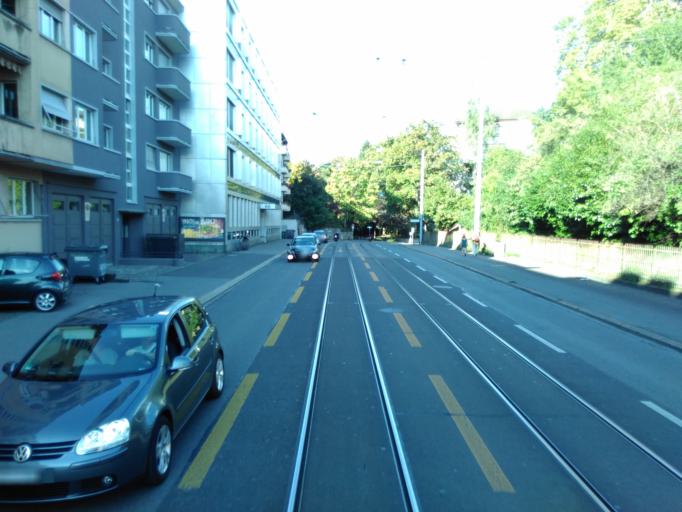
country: CH
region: Zurich
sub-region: Bezirk Zuerich
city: Zuerich (Kreis 2) / Enge
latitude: 47.3631
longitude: 8.5274
